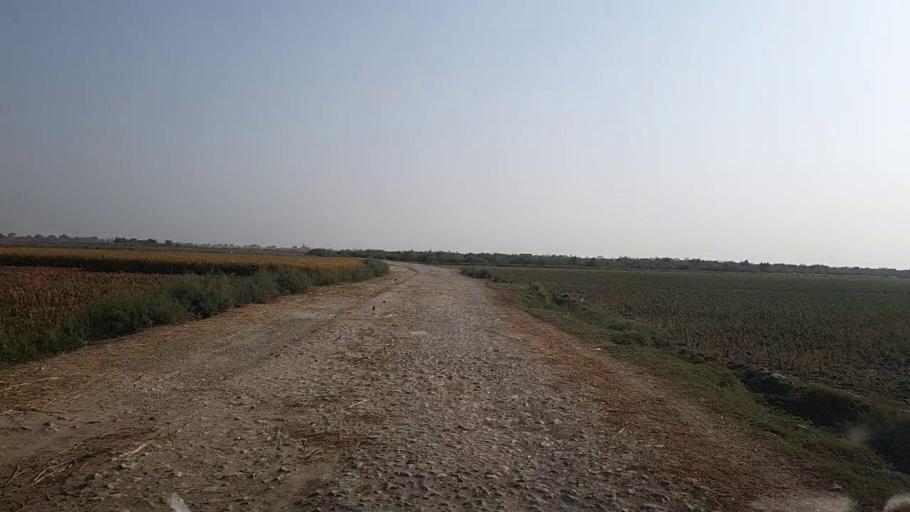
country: PK
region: Sindh
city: Kandhkot
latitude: 28.2969
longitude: 69.2524
